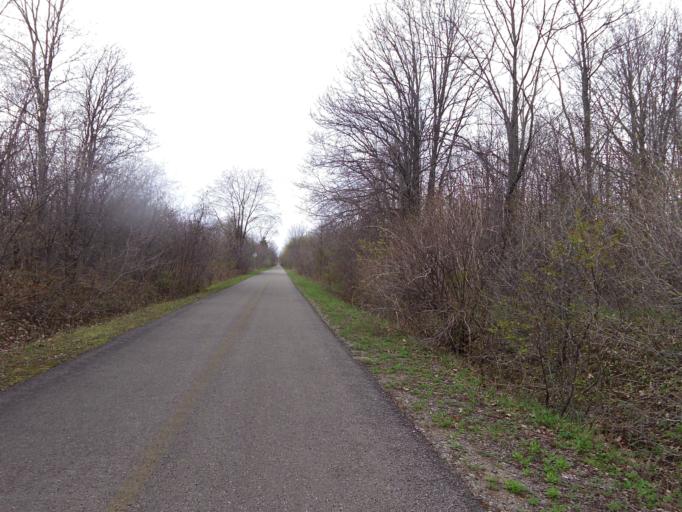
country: CA
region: Quebec
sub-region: Laurentides
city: Lachute
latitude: 45.5805
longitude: -74.4084
